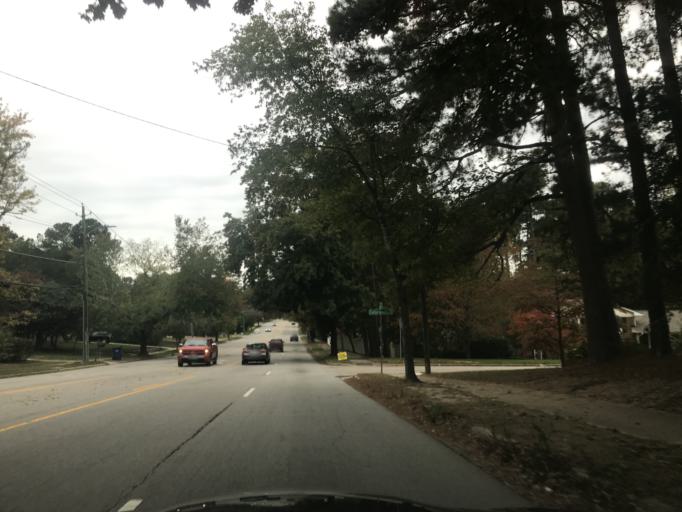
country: US
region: North Carolina
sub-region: Wake County
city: West Raleigh
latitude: 35.8517
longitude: -78.6282
